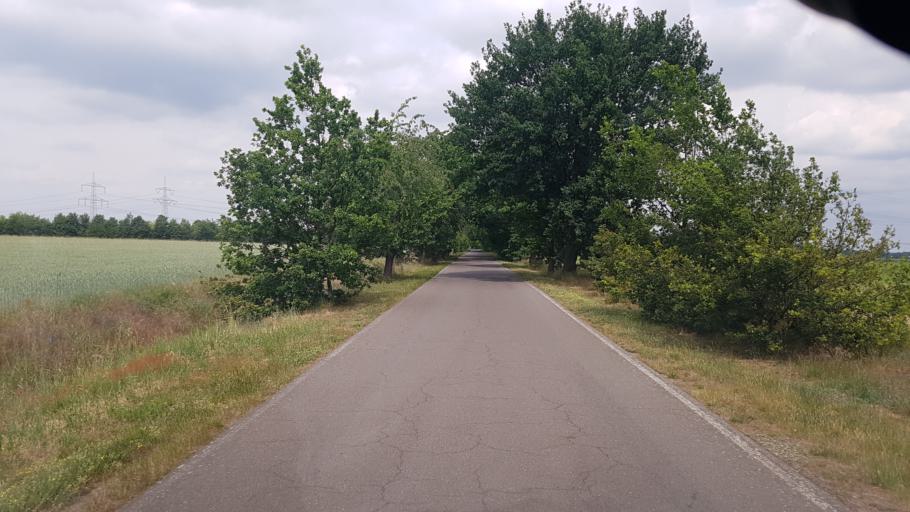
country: DE
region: Brandenburg
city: Dahme
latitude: 51.8472
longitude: 13.4420
